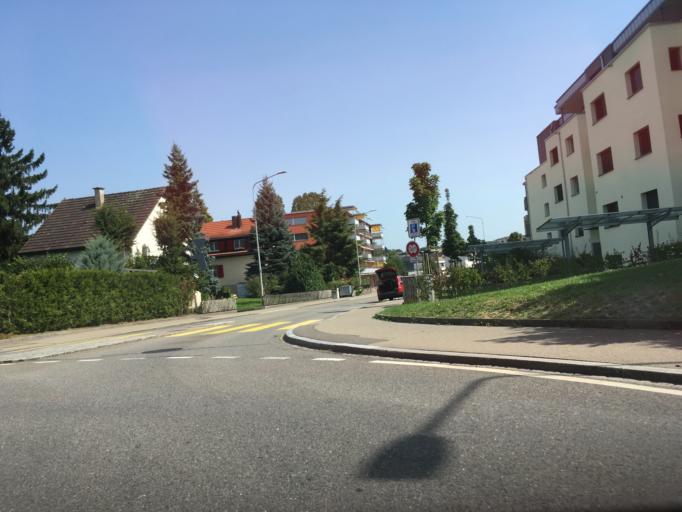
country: CH
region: Zurich
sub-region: Bezirk Buelach
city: Dietlikon / Eichwiesen
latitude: 47.4269
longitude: 8.6188
